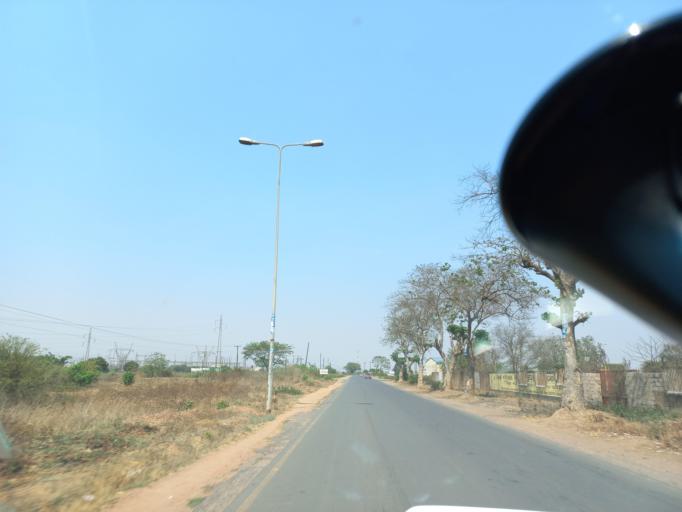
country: ZM
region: Lusaka
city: Kafue
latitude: -15.7486
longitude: 28.1645
